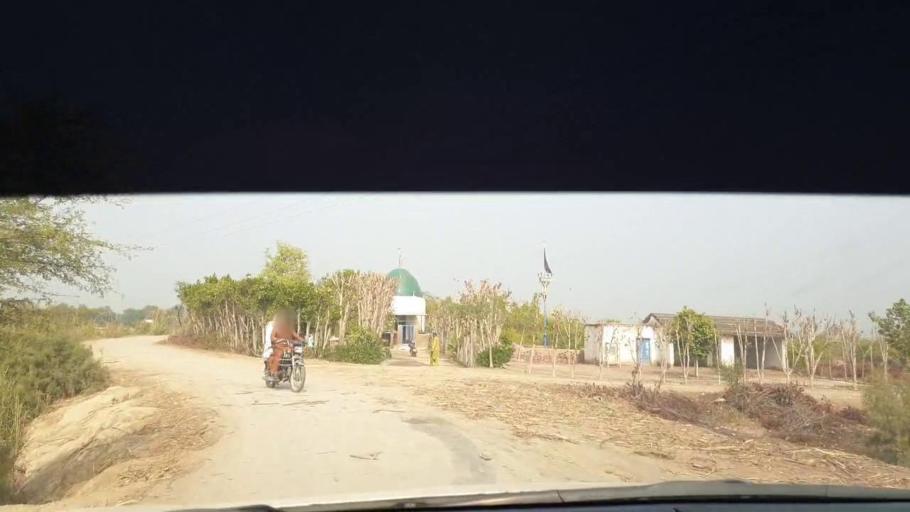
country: PK
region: Sindh
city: Berani
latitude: 25.8015
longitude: 68.8365
